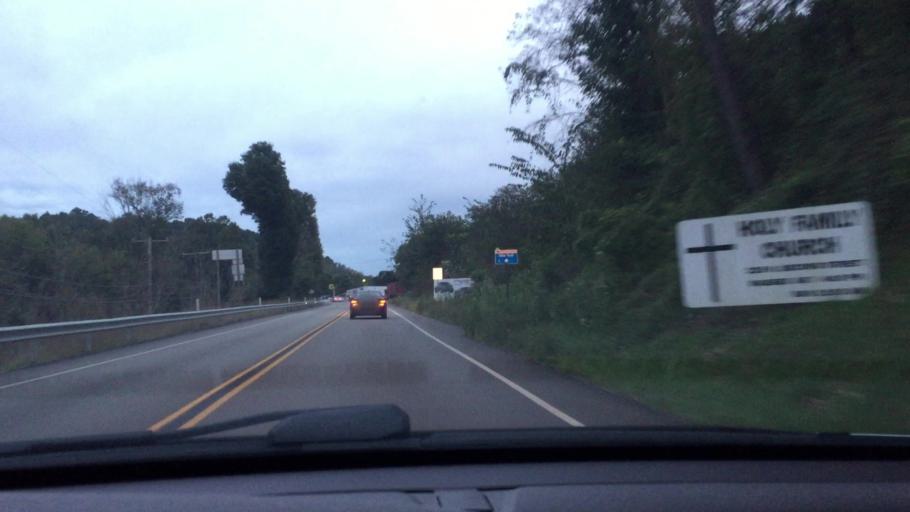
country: US
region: Pennsylvania
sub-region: Westmoreland County
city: West Newton
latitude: 40.2116
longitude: -79.7857
